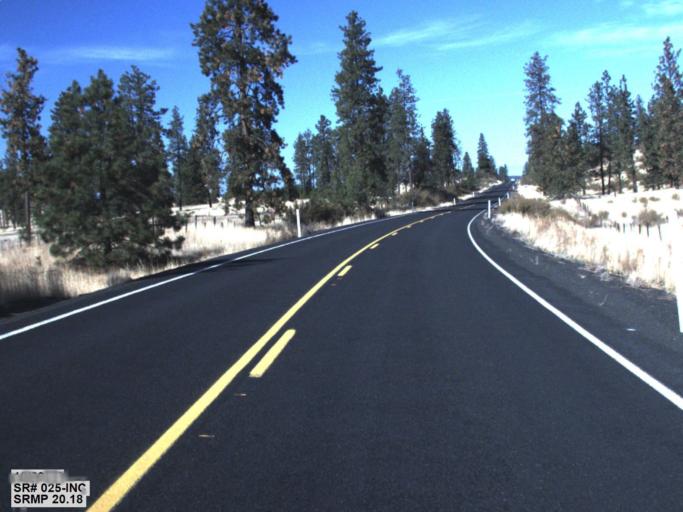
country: US
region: Washington
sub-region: Lincoln County
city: Davenport
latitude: 47.8964
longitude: -118.2739
